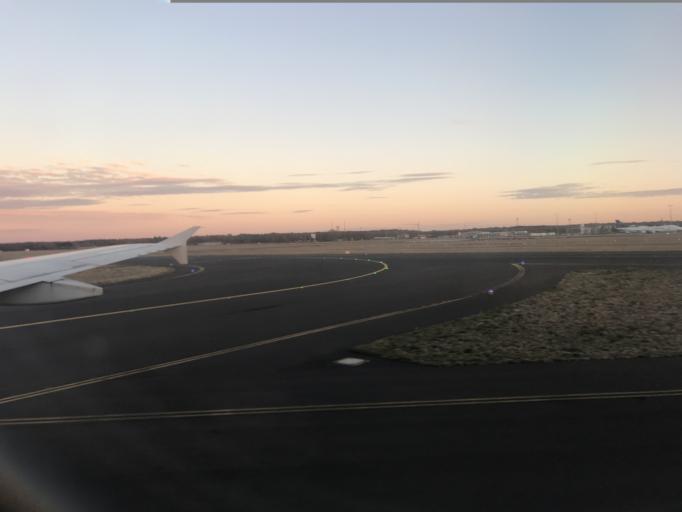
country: DE
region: Hesse
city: Morfelden-Walldorf
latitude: 50.0421
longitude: 8.5819
